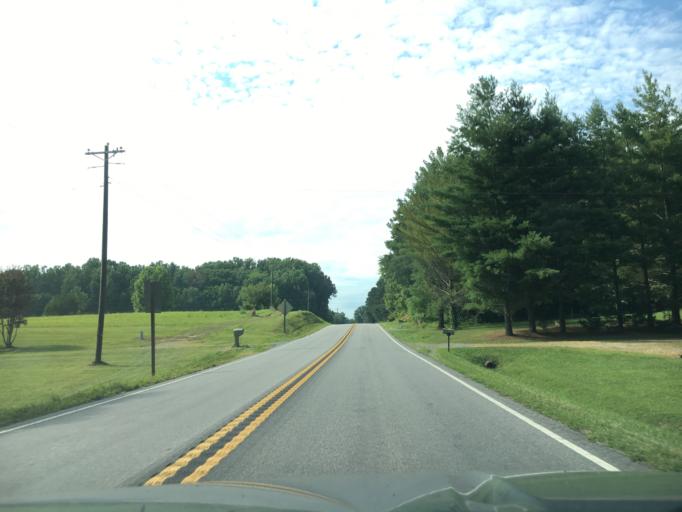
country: US
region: Virginia
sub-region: Halifax County
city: Mountain Road
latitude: 36.8707
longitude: -79.0126
